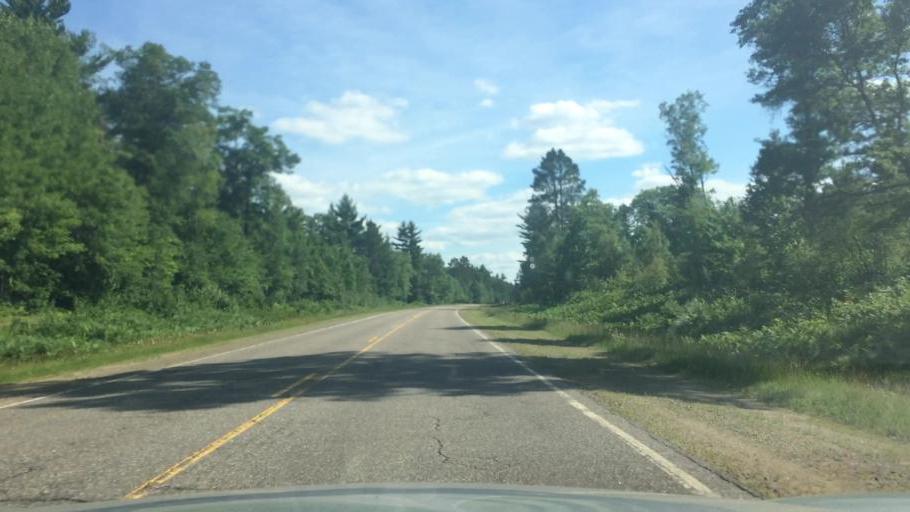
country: US
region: Wisconsin
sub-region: Vilas County
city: Lac du Flambeau
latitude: 46.0775
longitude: -89.6444
